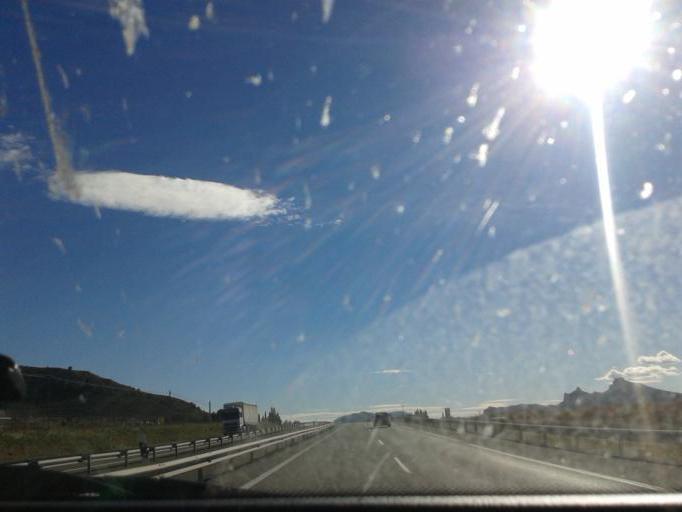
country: ES
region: Valencia
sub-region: Provincia de Alicante
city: Villena
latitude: 38.5953
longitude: -0.8454
